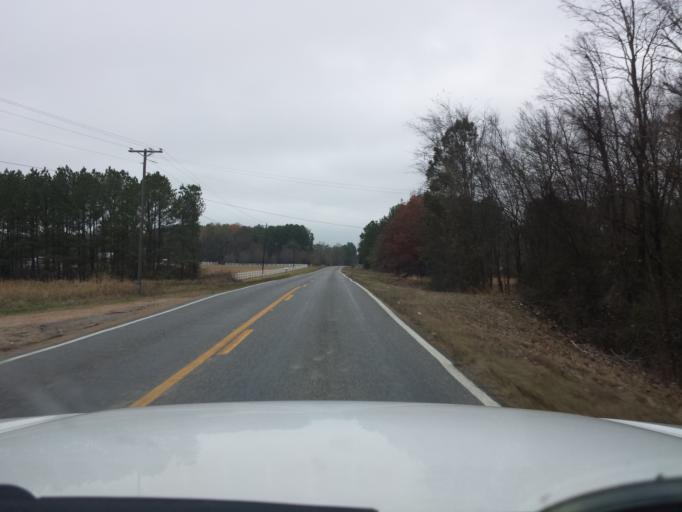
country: US
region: Mississippi
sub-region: Madison County
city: Canton
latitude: 32.4869
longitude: -89.9207
